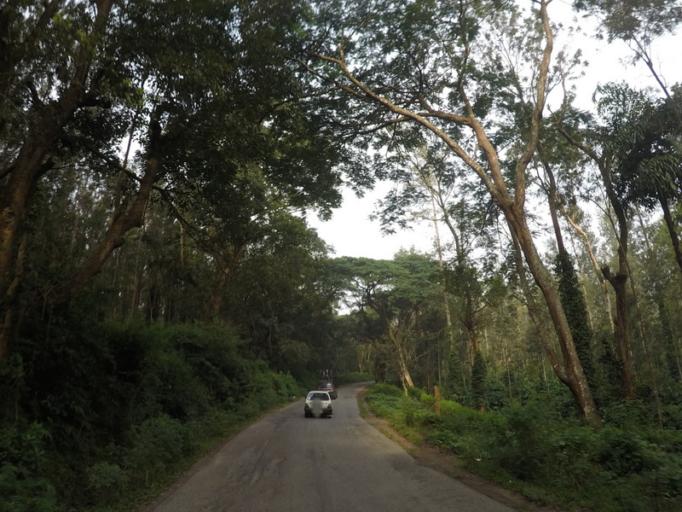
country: IN
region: Karnataka
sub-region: Chikmagalur
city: Chikmagalur
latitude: 13.2678
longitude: 75.7002
